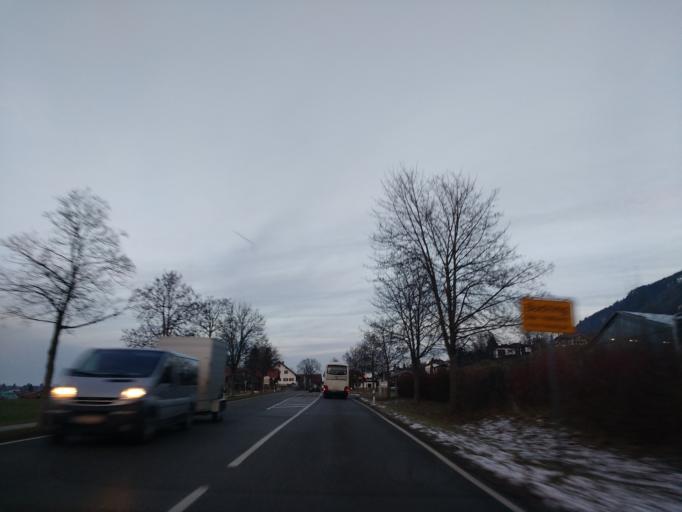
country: DE
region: Bavaria
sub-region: Swabia
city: Halblech
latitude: 47.6129
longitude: 10.8034
